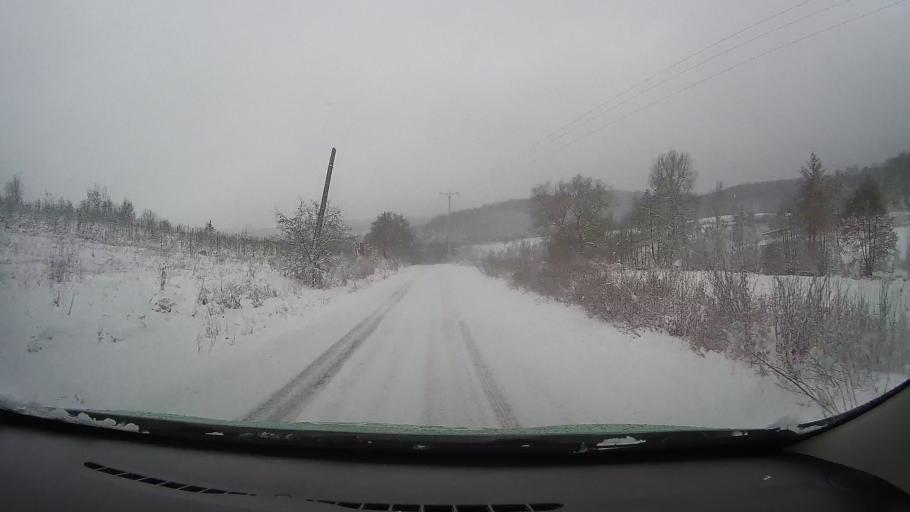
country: RO
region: Hunedoara
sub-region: Comuna Carjiti
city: Carjiti
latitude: 45.8337
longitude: 22.8406
